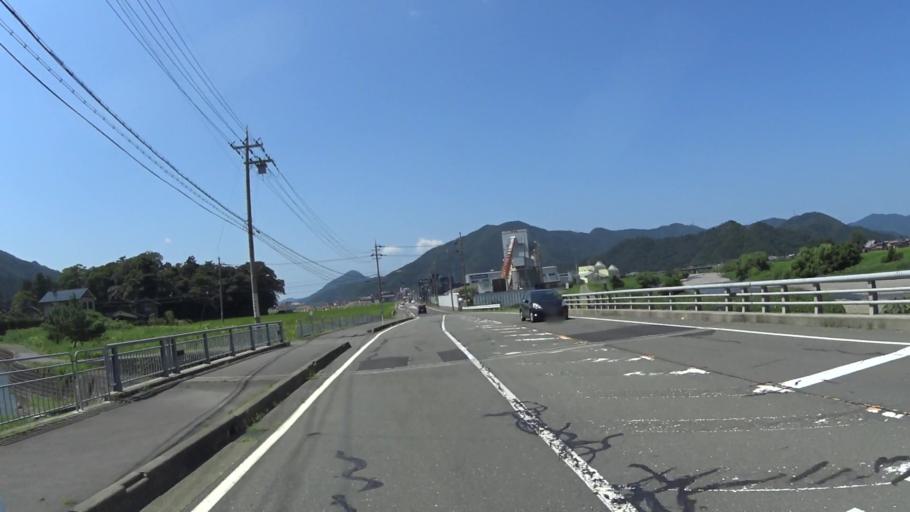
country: JP
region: Fukui
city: Obama
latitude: 35.4587
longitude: 135.8686
